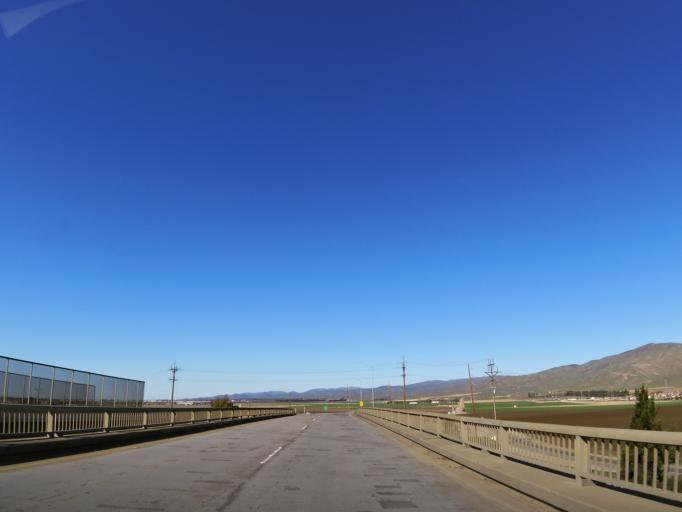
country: US
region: California
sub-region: Monterey County
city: Soledad
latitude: 36.4311
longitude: -121.3369
